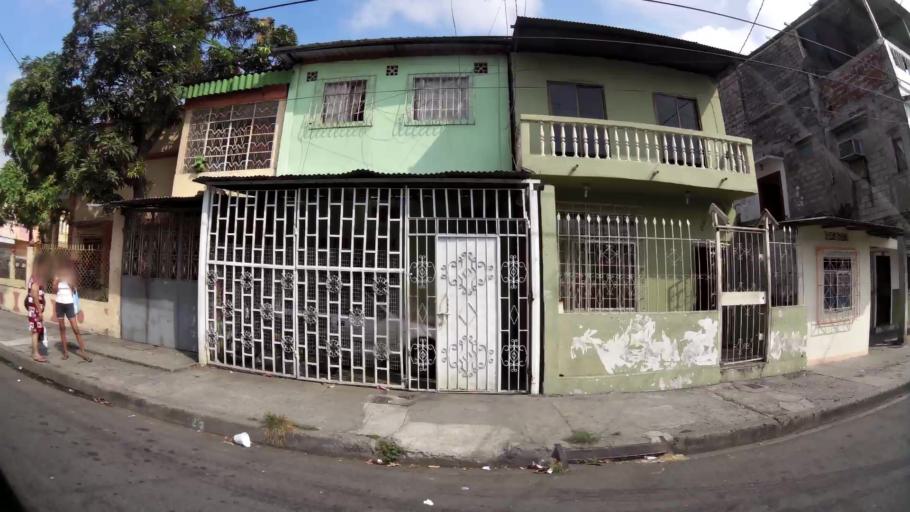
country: EC
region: Guayas
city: Guayaquil
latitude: -2.2133
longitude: -79.9045
